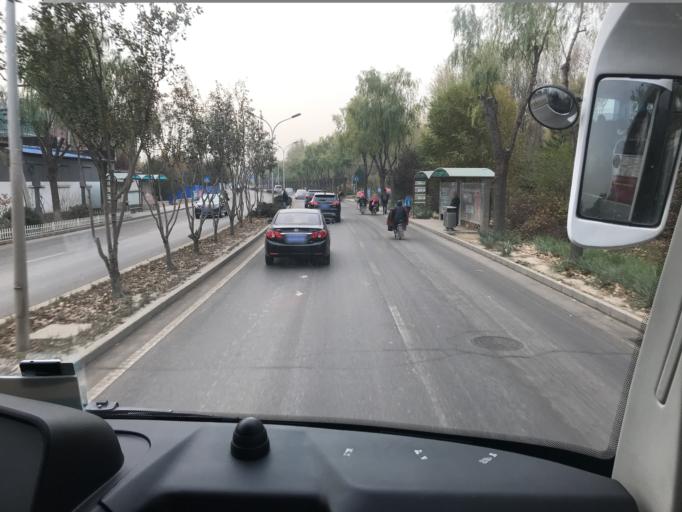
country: CN
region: Beijing
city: Sujiatuo
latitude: 40.0950
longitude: 116.2084
